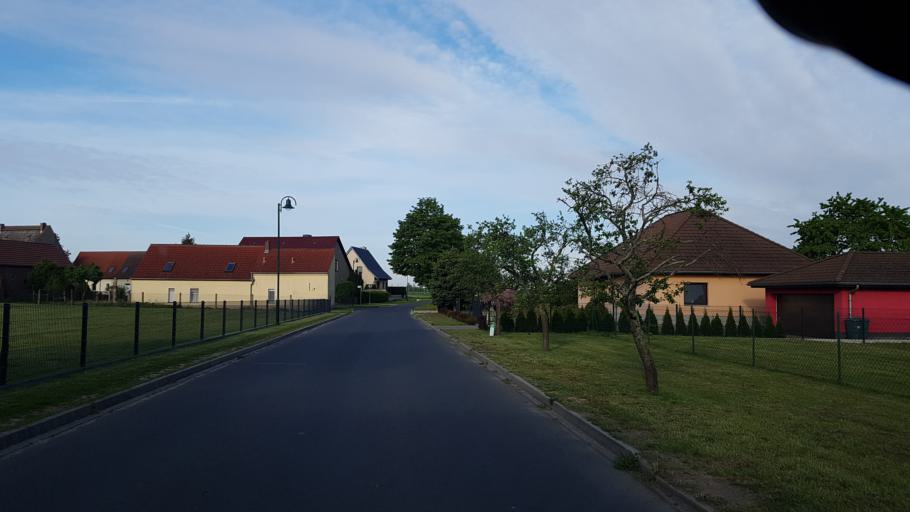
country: DE
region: Brandenburg
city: Dahme
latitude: 51.8627
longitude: 13.4614
